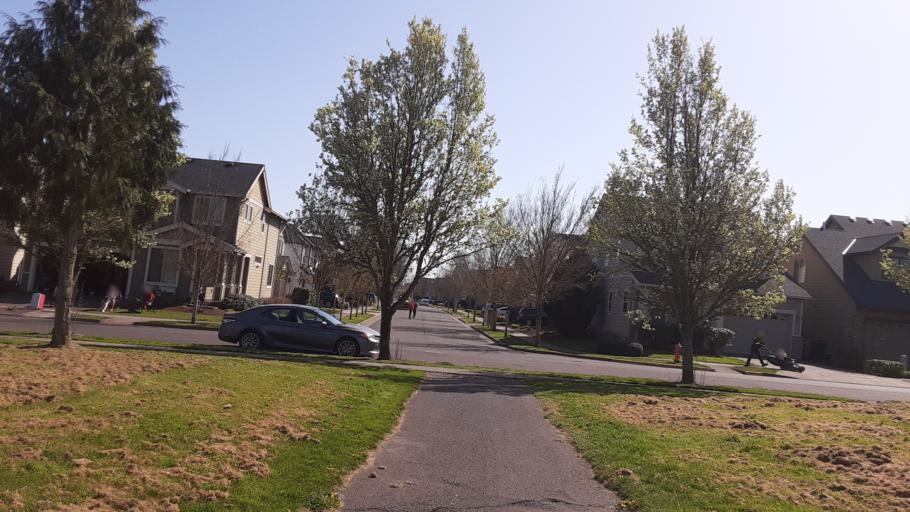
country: US
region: Oregon
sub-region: Benton County
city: Corvallis
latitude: 44.5302
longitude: -123.2610
